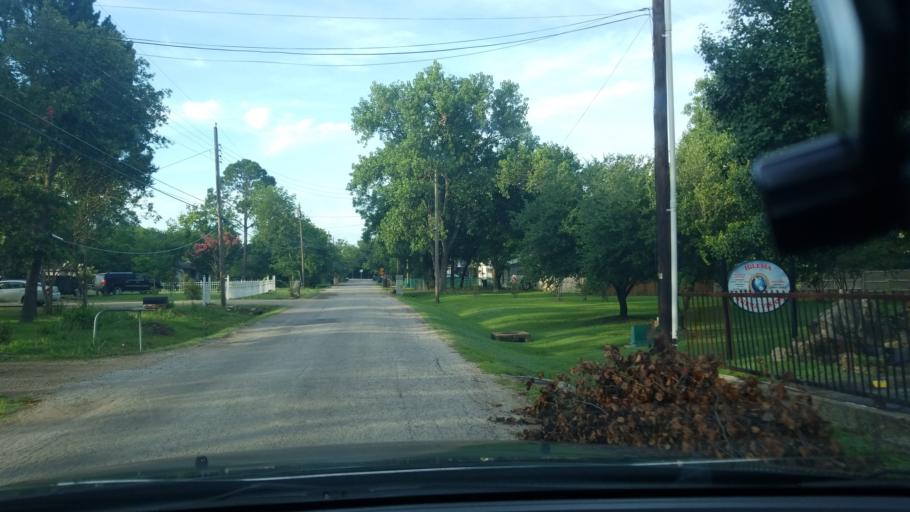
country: US
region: Texas
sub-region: Dallas County
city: Balch Springs
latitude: 32.7598
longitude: -96.6388
